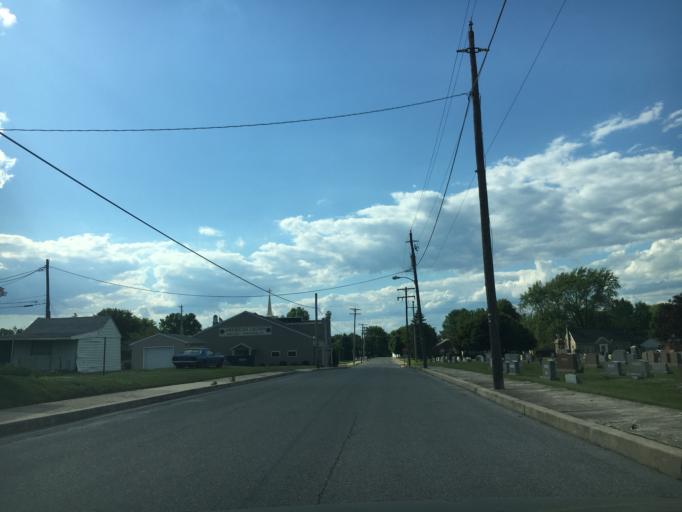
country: US
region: Pennsylvania
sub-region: Berks County
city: Fleetwood
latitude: 40.4566
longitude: -75.8163
